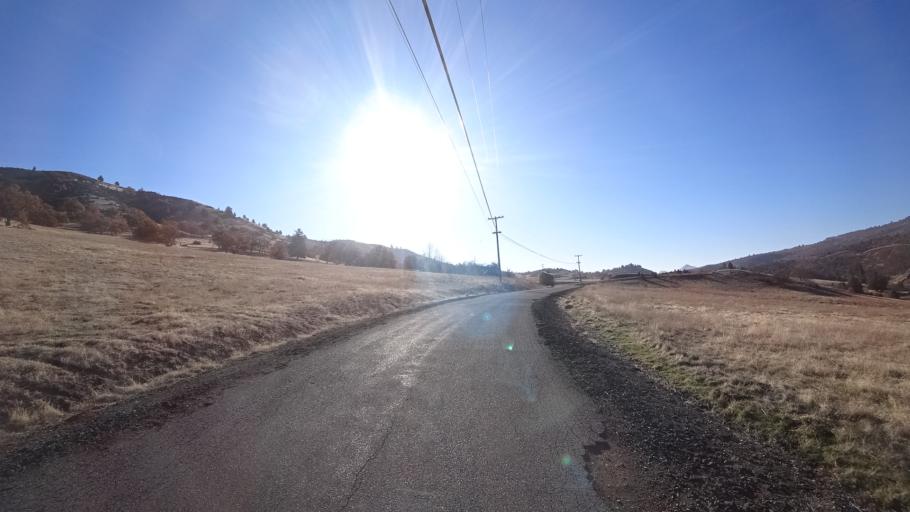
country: US
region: California
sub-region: Siskiyou County
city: Montague
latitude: 41.8888
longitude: -122.4763
